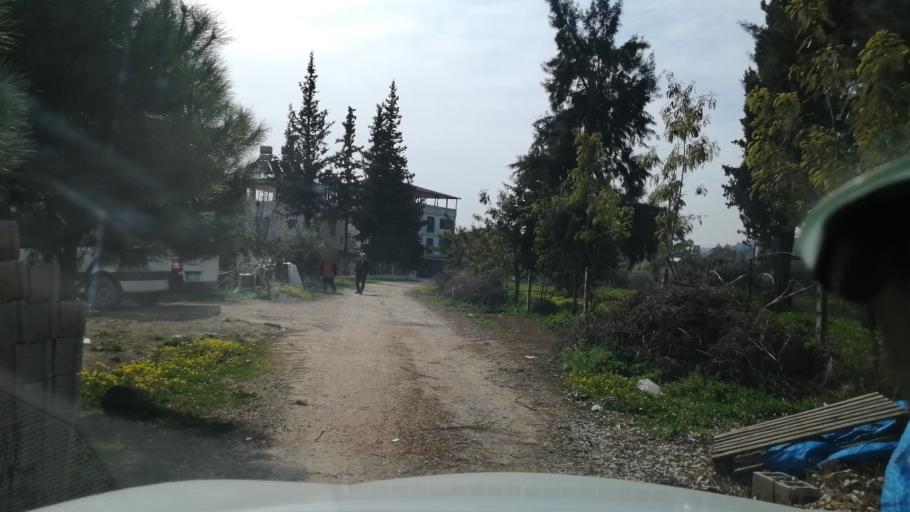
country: TR
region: Hatay
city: Serinyol
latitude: 36.3542
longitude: 36.2049
